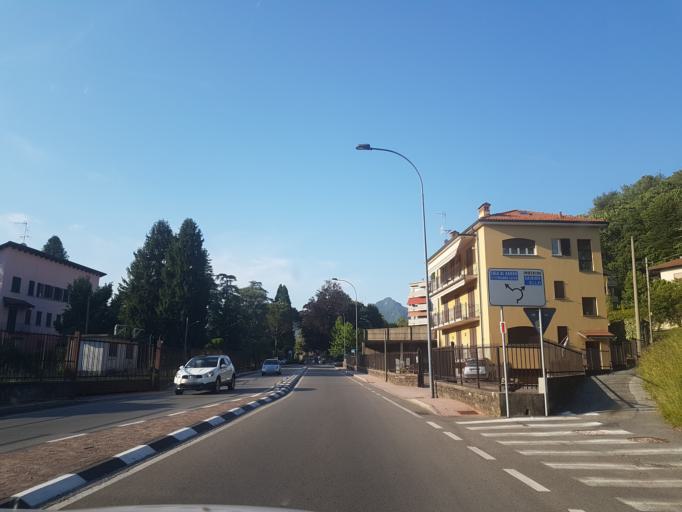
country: IT
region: Lombardy
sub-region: Provincia di Lecco
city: Oggiono
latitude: 45.7924
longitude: 9.3526
